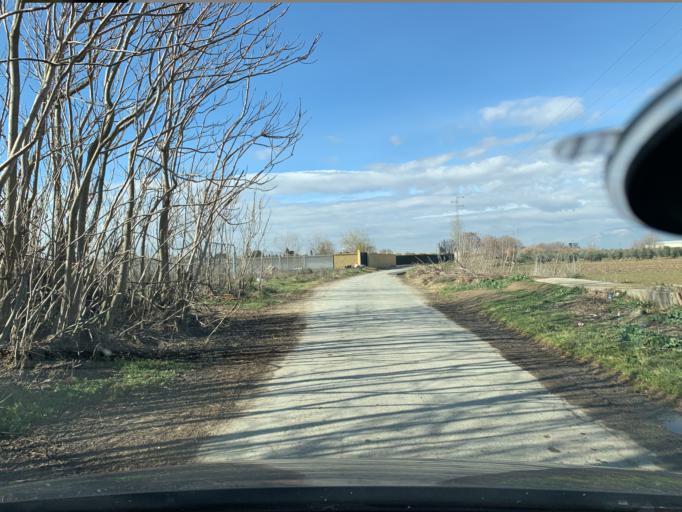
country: ES
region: Andalusia
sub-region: Provincia de Granada
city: Chauchina
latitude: 37.1894
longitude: -3.7524
